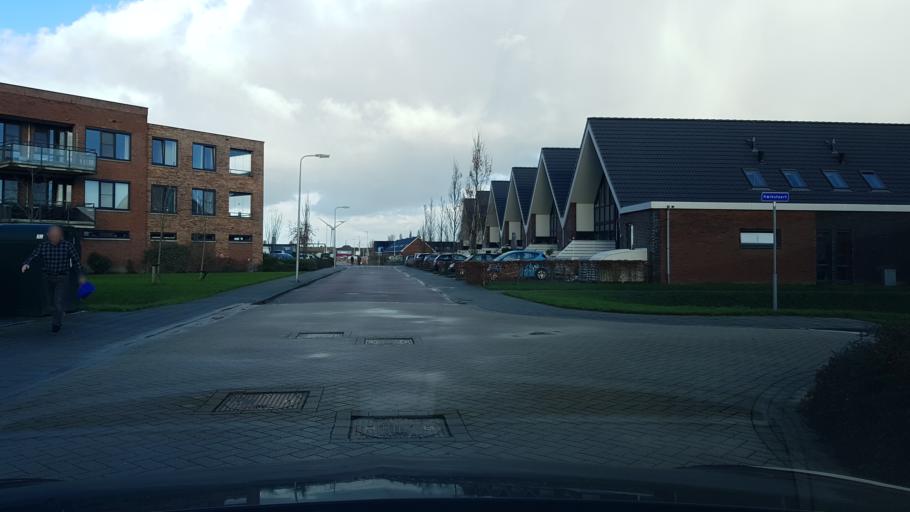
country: NL
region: South Holland
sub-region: Gemeente Kaag en Braassem
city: Leimuiden
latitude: 52.2218
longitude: 4.6592
